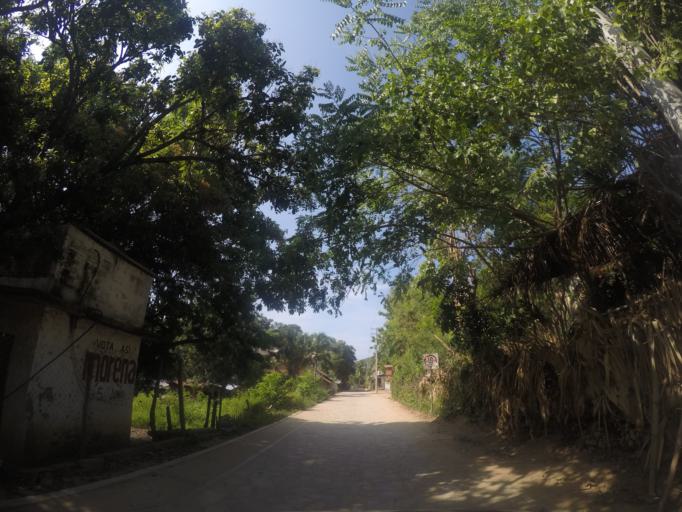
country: MX
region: Oaxaca
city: Santa Maria Tonameca
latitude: 15.6669
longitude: -96.5558
